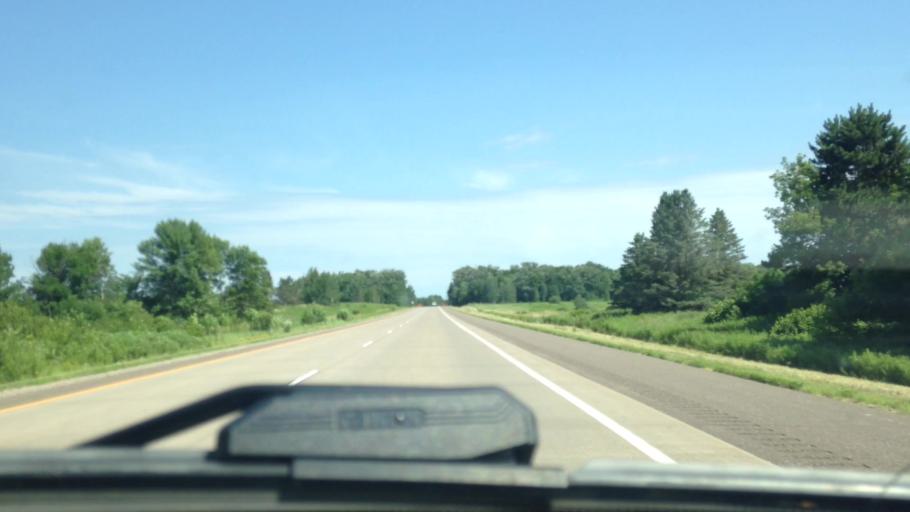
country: US
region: Wisconsin
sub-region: Barron County
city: Rice Lake
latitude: 45.5479
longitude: -91.7632
